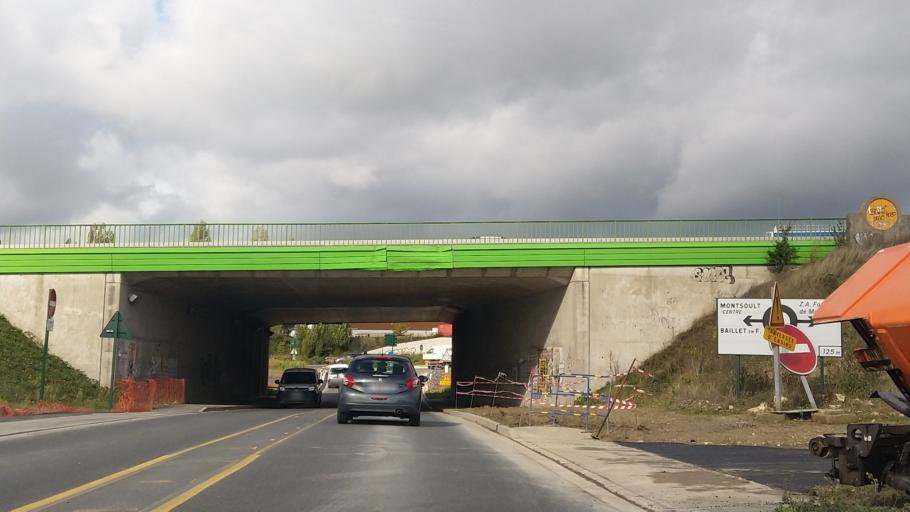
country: FR
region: Ile-de-France
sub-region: Departement du Val-d'Oise
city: Montsoult
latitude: 49.0623
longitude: 2.3277
